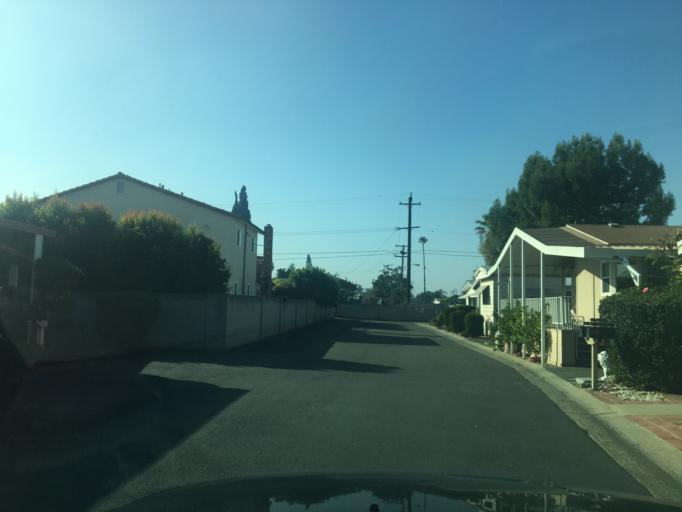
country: US
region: California
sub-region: Orange County
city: Tustin
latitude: 33.7365
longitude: -117.8277
